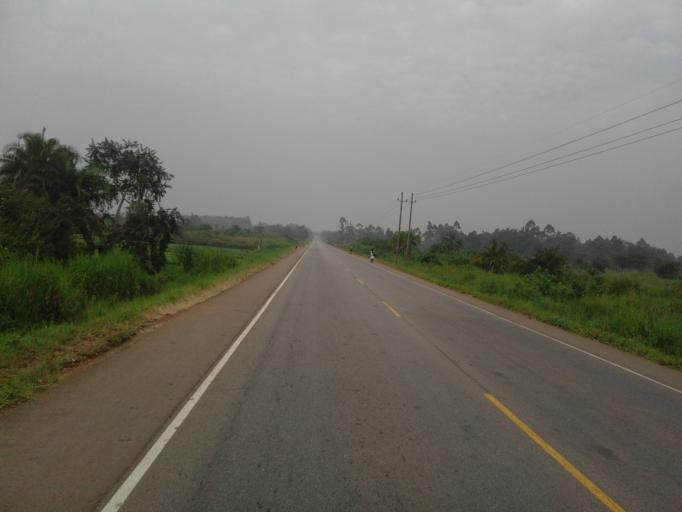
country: UG
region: Eastern Region
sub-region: Bugiri District
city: Bugiri
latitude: 0.5188
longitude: 33.8254
